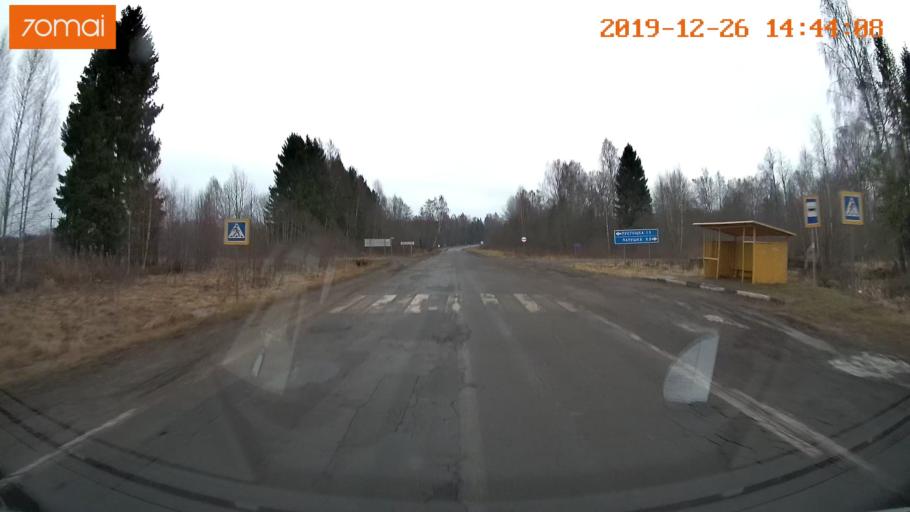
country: RU
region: Jaroslavl
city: Poshekhon'ye
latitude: 58.3508
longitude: 39.0476
